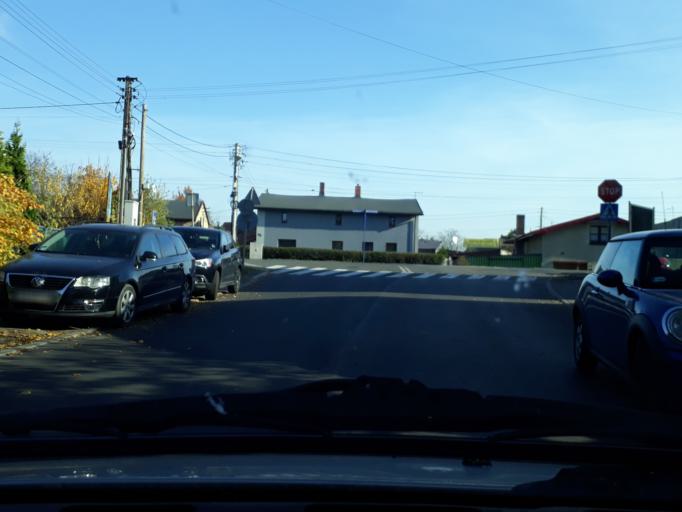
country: PL
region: Silesian Voivodeship
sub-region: Powiat tarnogorski
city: Tarnowskie Gory
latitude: 50.4234
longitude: 18.8670
